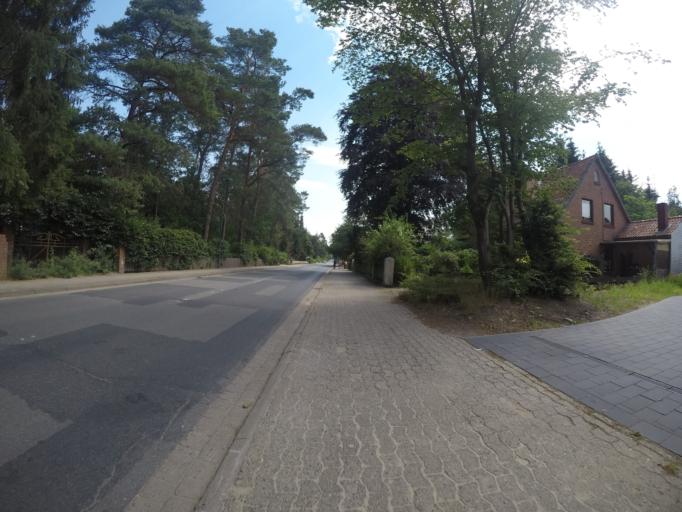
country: DE
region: Lower Saxony
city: Buchholz in der Nordheide
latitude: 53.2863
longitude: 9.8642
